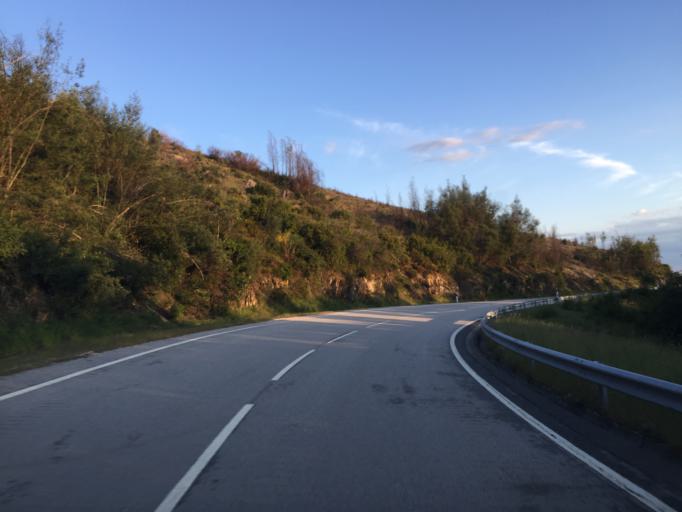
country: PT
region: Coimbra
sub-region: Pampilhosa da Serra
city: Pampilhosa da Serra
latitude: 40.0900
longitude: -7.9912
